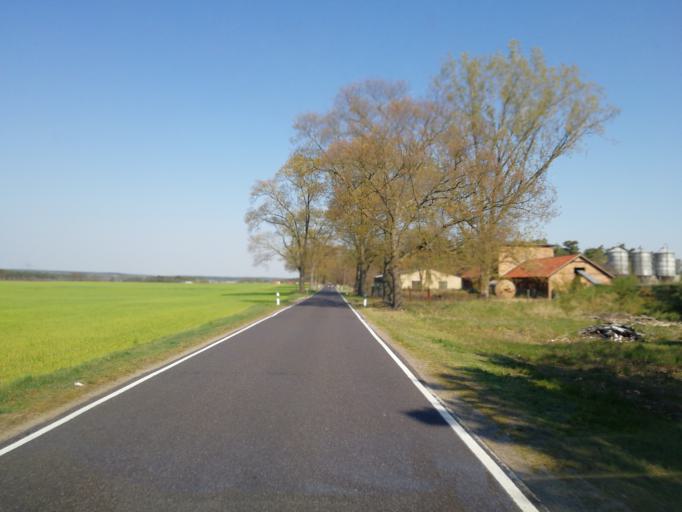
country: DE
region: Brandenburg
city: Bronkow
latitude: 51.7162
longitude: 13.8637
